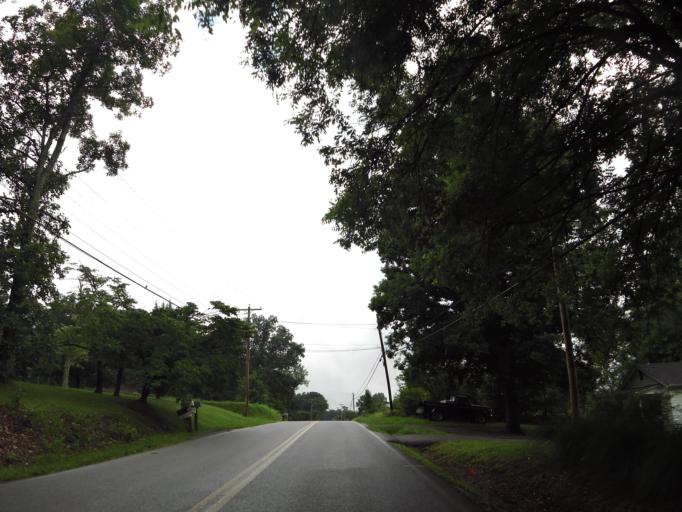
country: US
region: Tennessee
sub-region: Blount County
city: Eagleton Village
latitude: 35.7930
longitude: -83.9117
